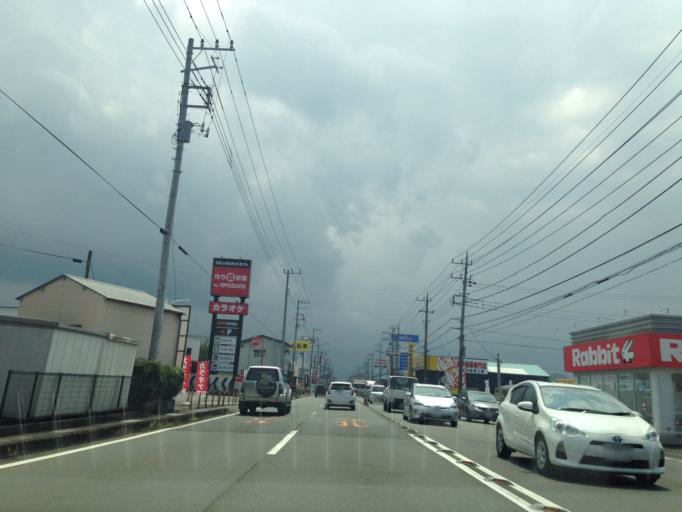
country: JP
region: Shizuoka
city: Mishima
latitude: 35.1054
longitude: 138.9210
